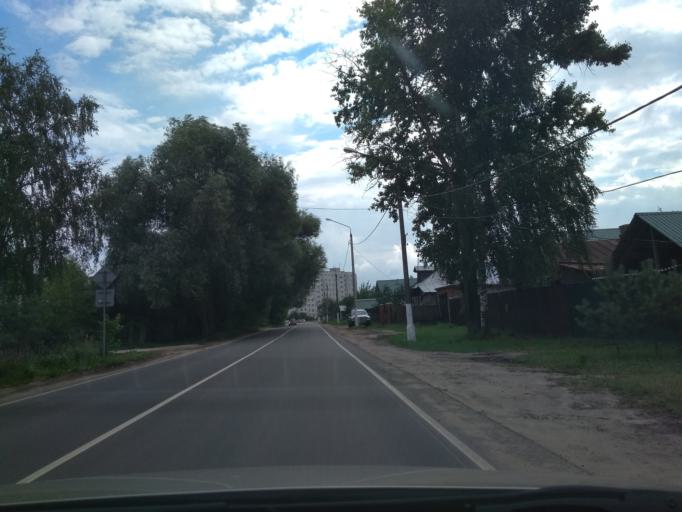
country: RU
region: Moskovskaya
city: Orekhovo-Zuyevo
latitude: 55.7947
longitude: 38.9384
